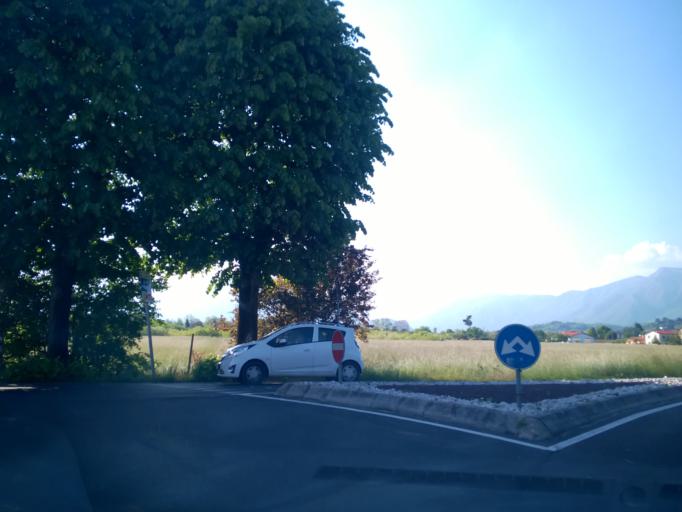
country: IT
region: Veneto
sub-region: Provincia di Vicenza
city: Grumolo Pedemonte
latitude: 45.7153
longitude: 11.4881
